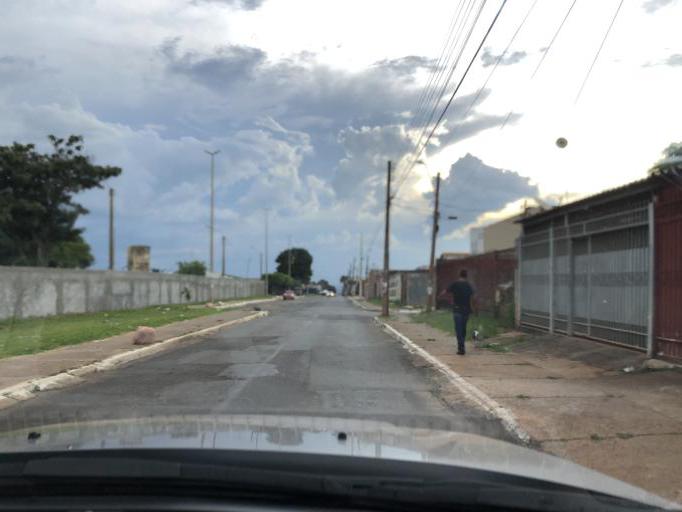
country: BR
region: Federal District
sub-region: Brasilia
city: Brasilia
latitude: -15.8202
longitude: -48.1046
